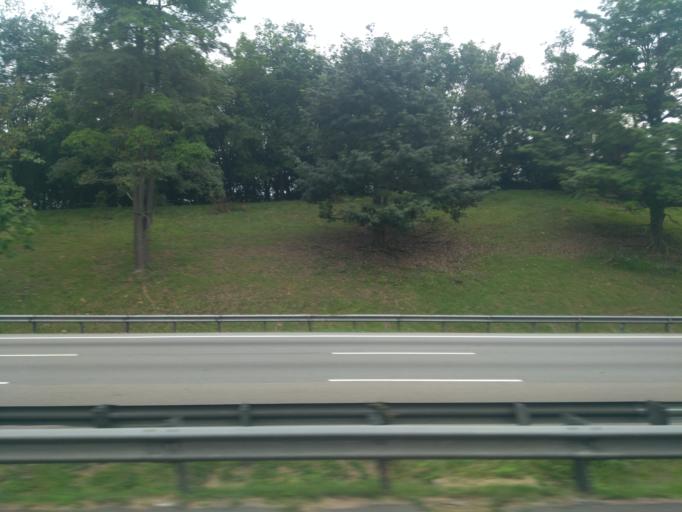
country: MY
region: Melaka
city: Pulau Sebang
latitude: 2.4484
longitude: 102.1724
